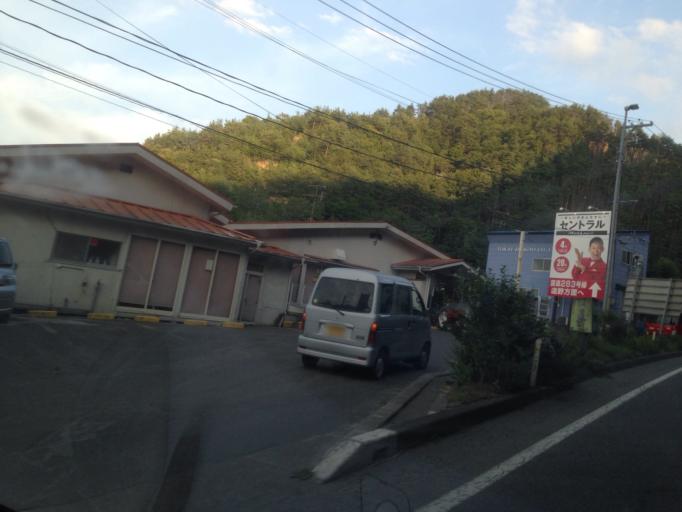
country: JP
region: Iwate
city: Otsuchi
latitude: 39.3529
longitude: 141.8932
